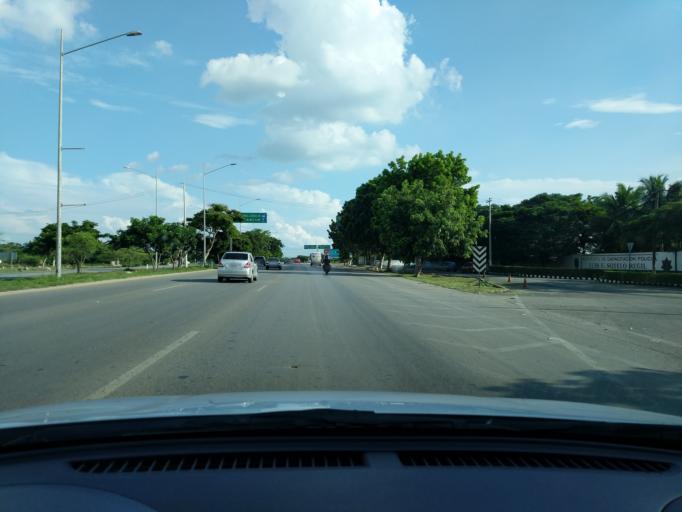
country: MX
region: Yucatan
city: Itzincab Palomeque
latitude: 20.9233
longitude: -89.6877
